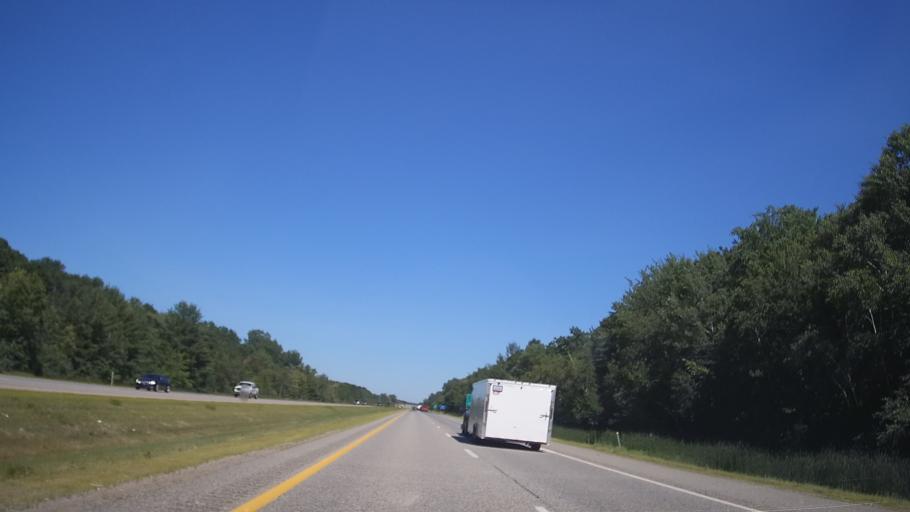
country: US
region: Michigan
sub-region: Midland County
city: Midland
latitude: 43.6561
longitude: -84.2879
